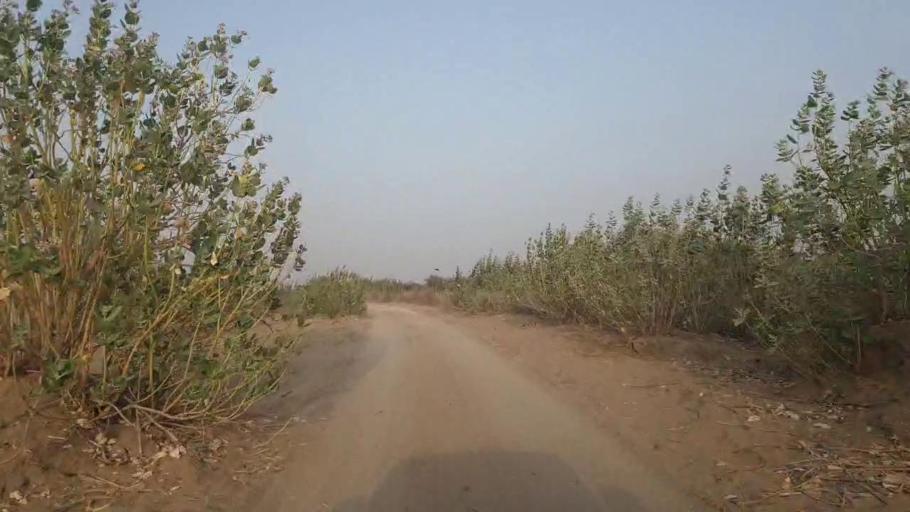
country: PK
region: Sindh
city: Chor
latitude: 25.5195
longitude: 69.9524
